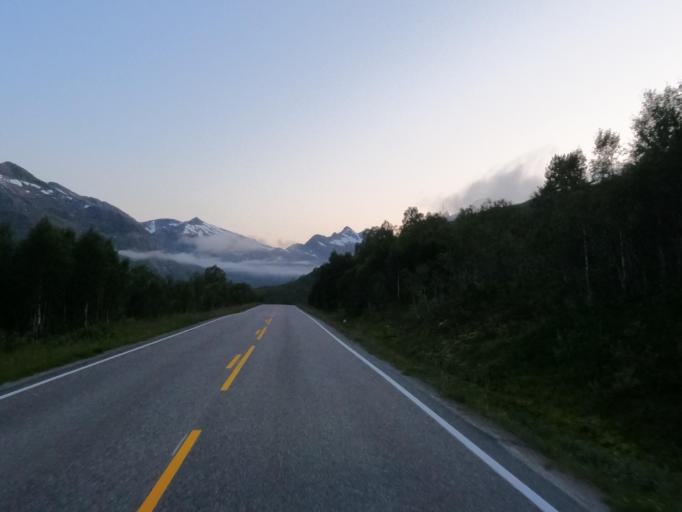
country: NO
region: Nordland
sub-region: Lodingen
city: Lodingen
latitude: 68.5323
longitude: 15.7971
